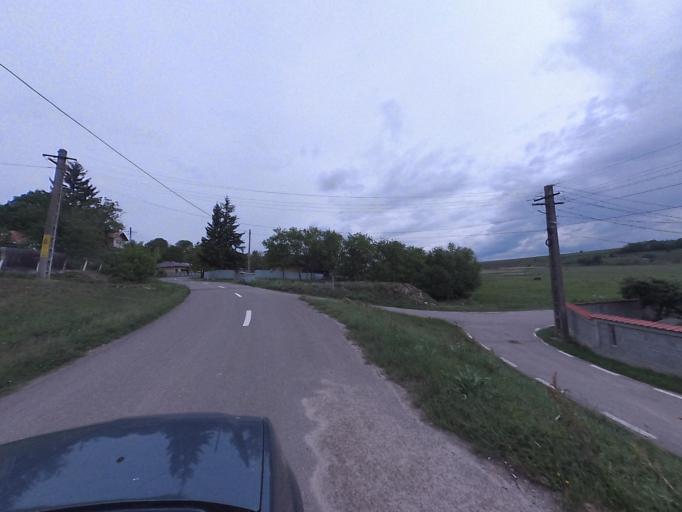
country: RO
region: Neamt
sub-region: Comuna Dulcesti
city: Dulcesti
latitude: 46.9569
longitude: 26.7974
